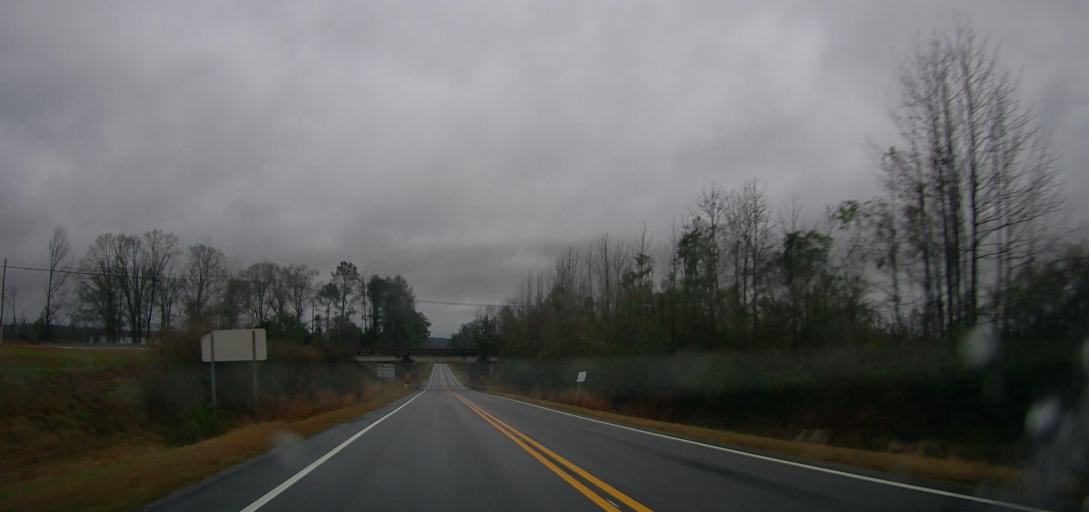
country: US
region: Alabama
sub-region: Chilton County
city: Thorsby
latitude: 32.7679
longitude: -86.8790
